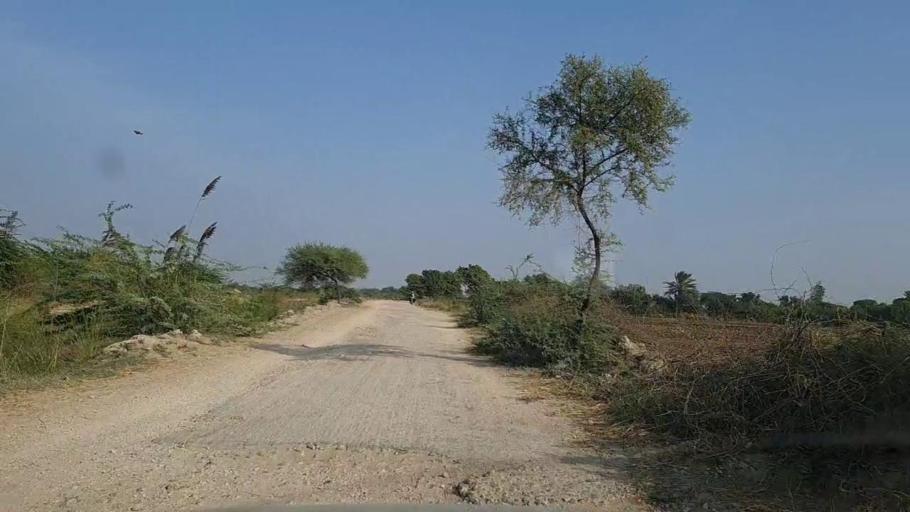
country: PK
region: Sindh
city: Mirpur Sakro
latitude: 24.5967
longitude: 67.5936
